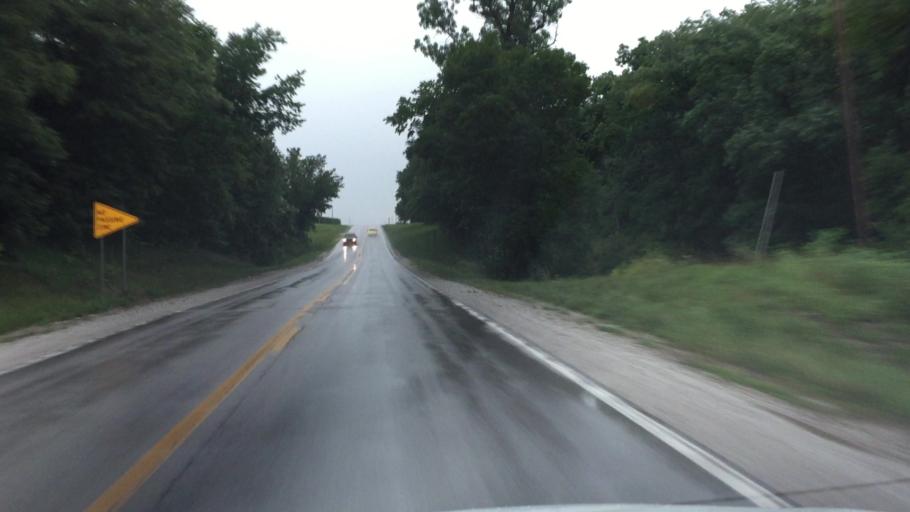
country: US
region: Illinois
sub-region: Hancock County
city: Carthage
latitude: 40.4397
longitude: -91.1400
